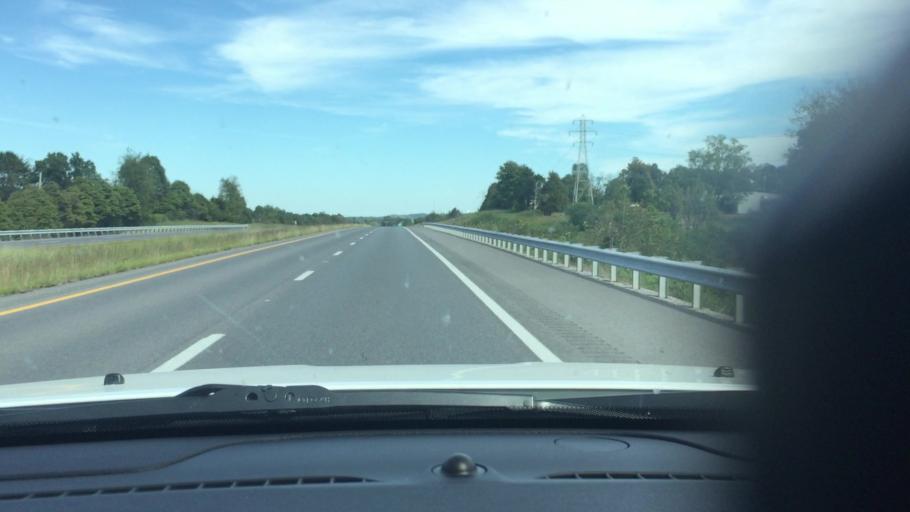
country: US
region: Kentucky
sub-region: Caldwell County
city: Princeton
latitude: 37.1108
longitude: -87.9455
